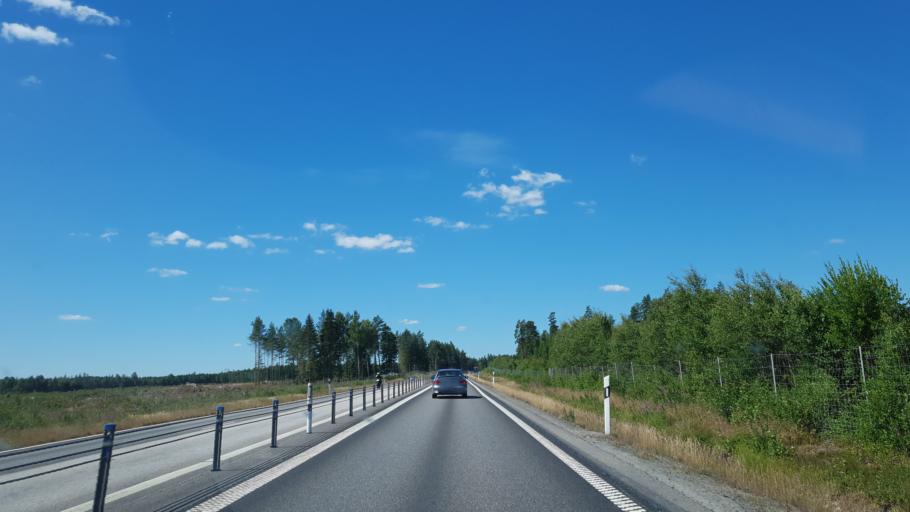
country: SE
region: Kronoberg
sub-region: Alvesta Kommun
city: Alvesta
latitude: 56.9177
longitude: 14.5183
